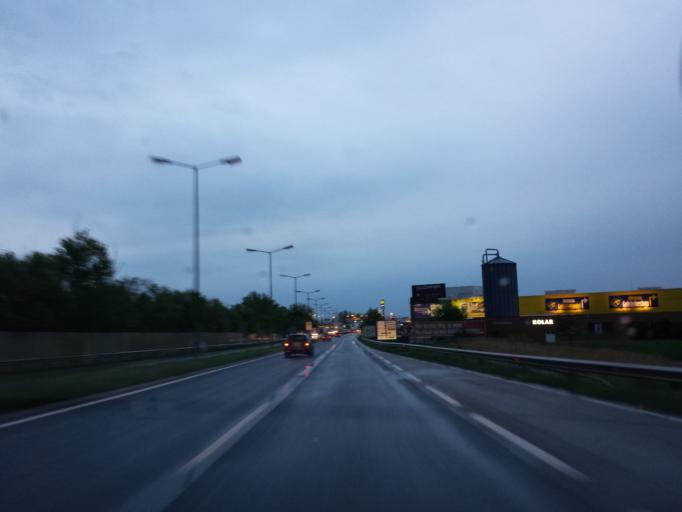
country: AT
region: Lower Austria
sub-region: Politischer Bezirk Modling
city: Brunn am Gebirge
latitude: 48.1151
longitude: 16.3008
